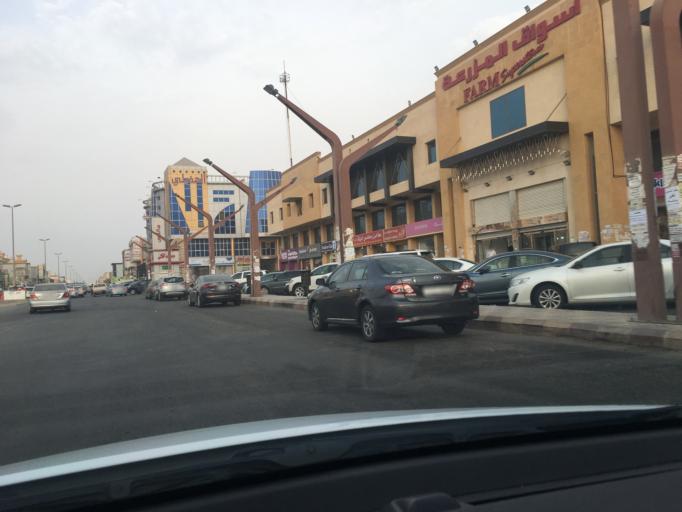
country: SA
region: Makkah
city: Jeddah
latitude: 21.7571
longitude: 39.1857
